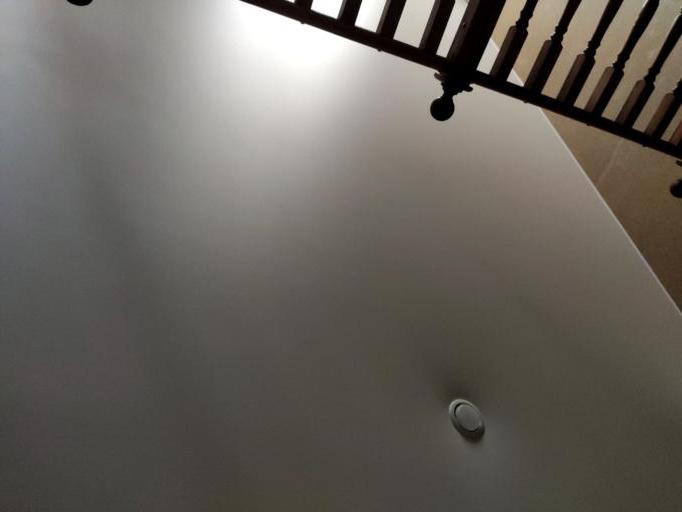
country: RU
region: Krasnodarskiy
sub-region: Sochi City
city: Khosta
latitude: 43.5424
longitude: 39.8059
